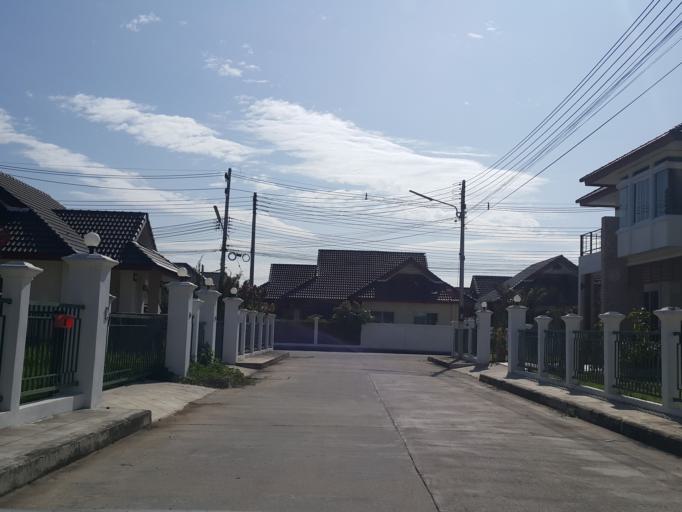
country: TH
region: Chiang Mai
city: Saraphi
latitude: 18.7752
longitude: 99.0515
